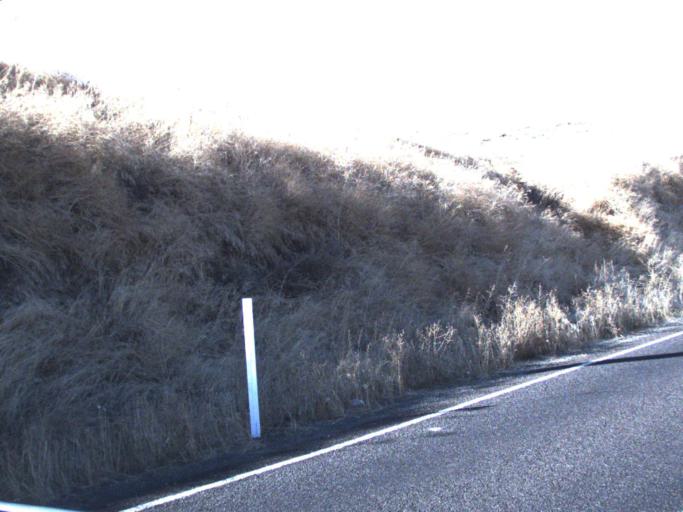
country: US
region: Washington
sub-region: Walla Walla County
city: Walla Walla
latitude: 46.1458
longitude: -118.3726
